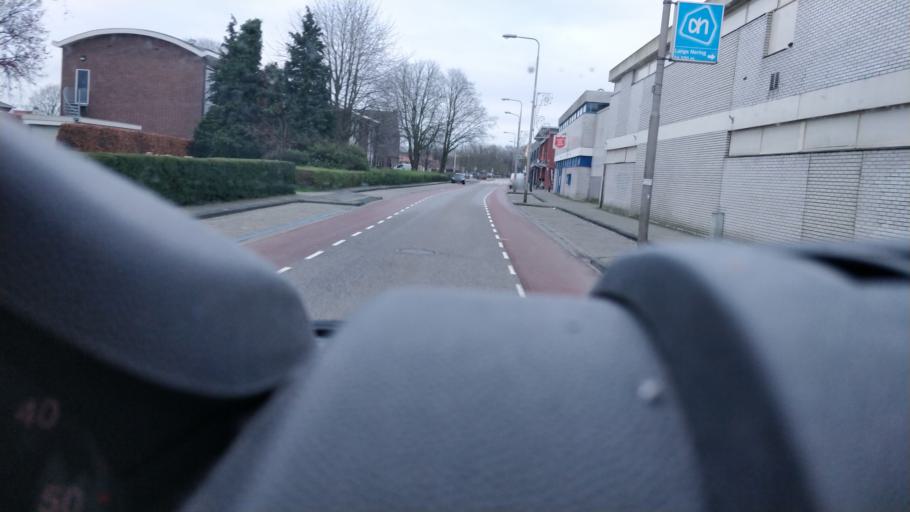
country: NL
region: Flevoland
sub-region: Gemeente Noordoostpolder
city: Emmeloord
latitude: 52.7120
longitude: 5.7547
